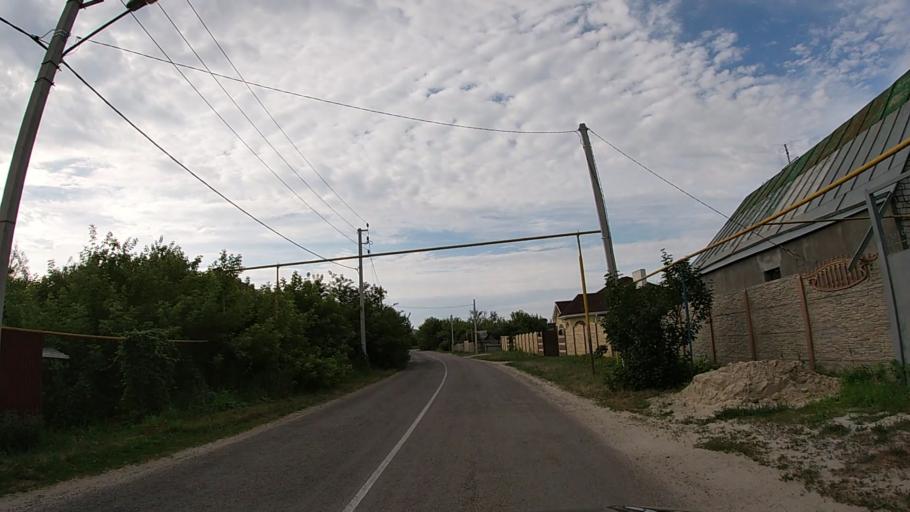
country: RU
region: Belgorod
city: Severnyy
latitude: 50.7095
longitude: 36.5987
